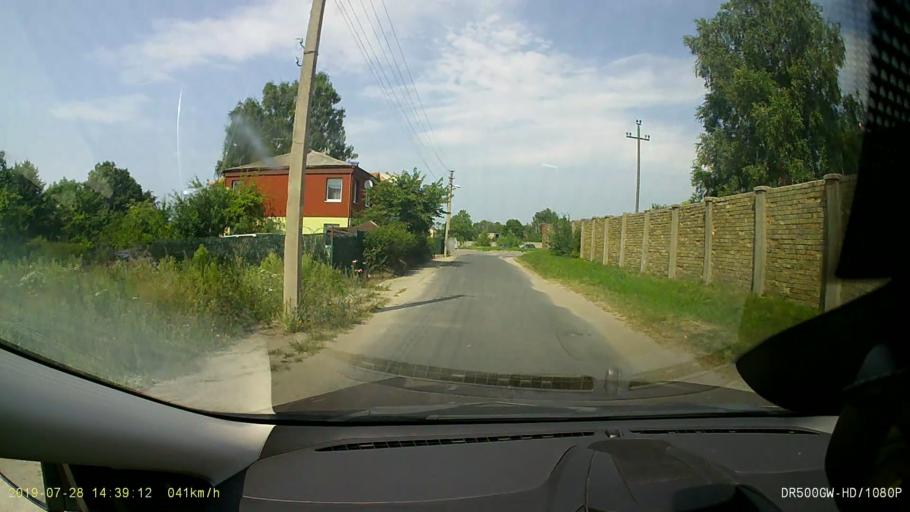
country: RU
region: Kaliningrad
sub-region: Gorod Kaliningrad
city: Yantarnyy
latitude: 54.8749
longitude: 19.9394
